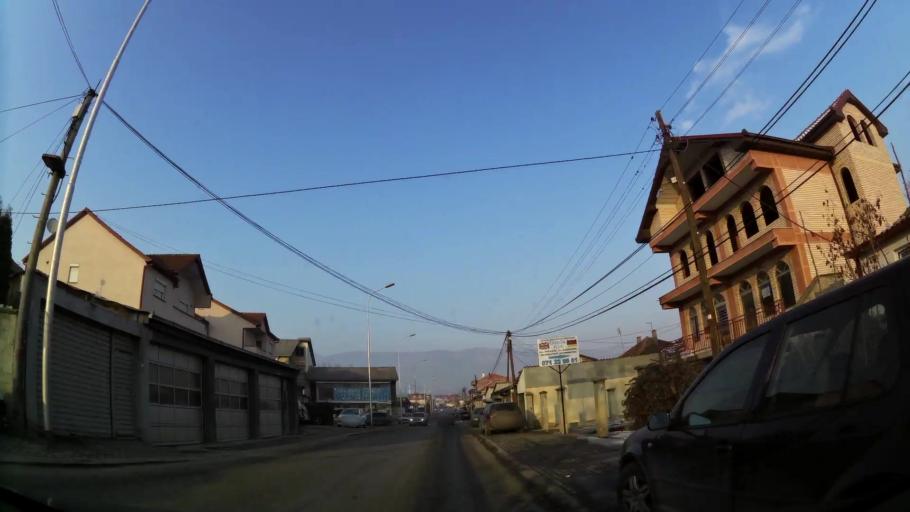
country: MK
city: Creshevo
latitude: 42.0137
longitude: 21.5105
